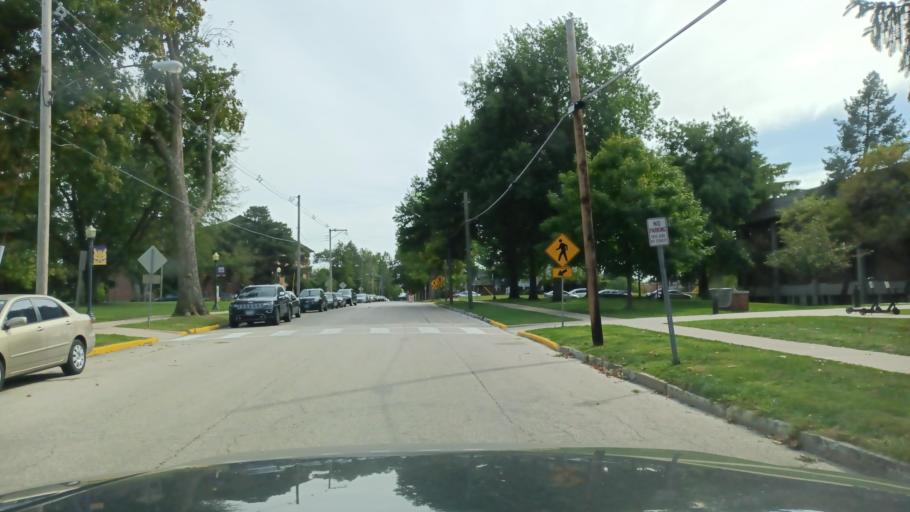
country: US
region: Illinois
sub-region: Knox County
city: Galesburg
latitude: 40.9434
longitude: -90.3744
